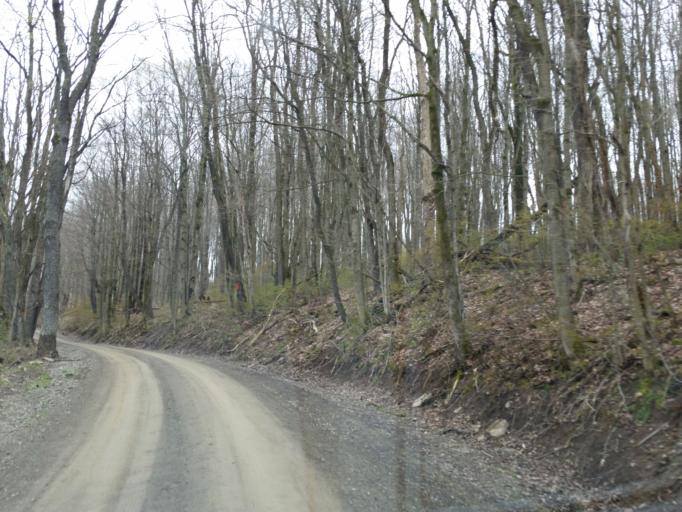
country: US
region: New York
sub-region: Allegany County
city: Andover
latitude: 42.0396
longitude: -77.7422
